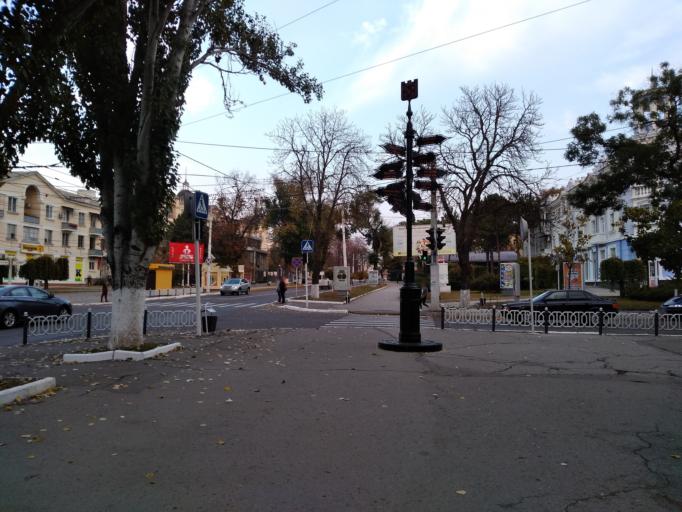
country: MD
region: Telenesti
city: Tiraspolul Nou
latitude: 46.8362
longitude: 29.6209
